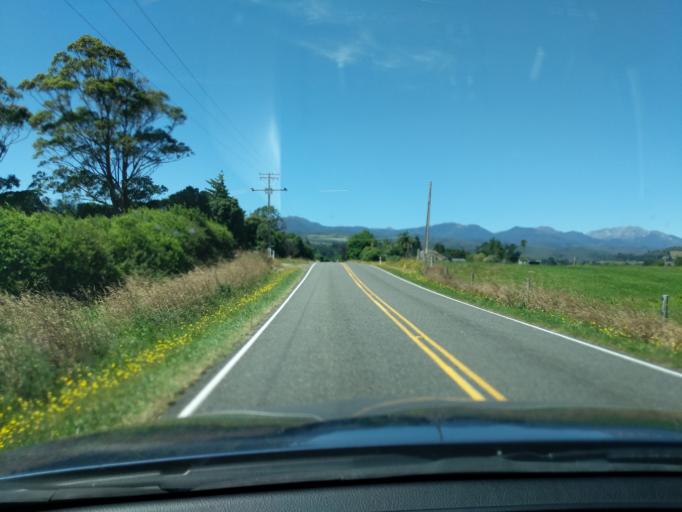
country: NZ
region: Tasman
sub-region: Tasman District
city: Takaka
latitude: -40.7116
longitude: 172.6374
